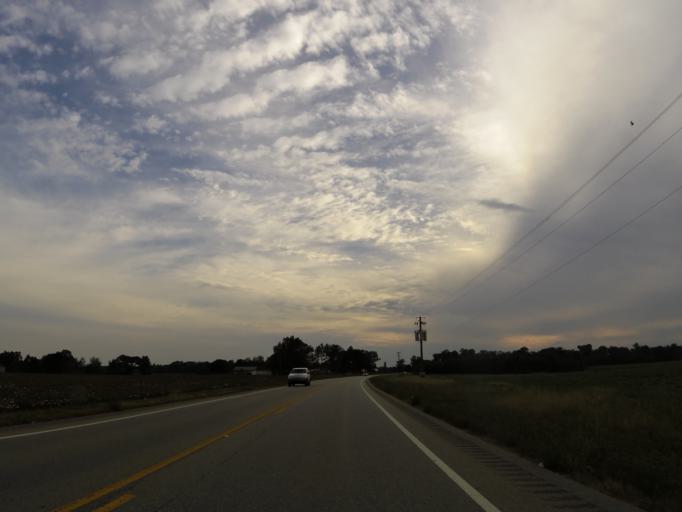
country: US
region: Alabama
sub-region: Monroe County
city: Frisco City
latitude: 31.3296
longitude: -87.4585
